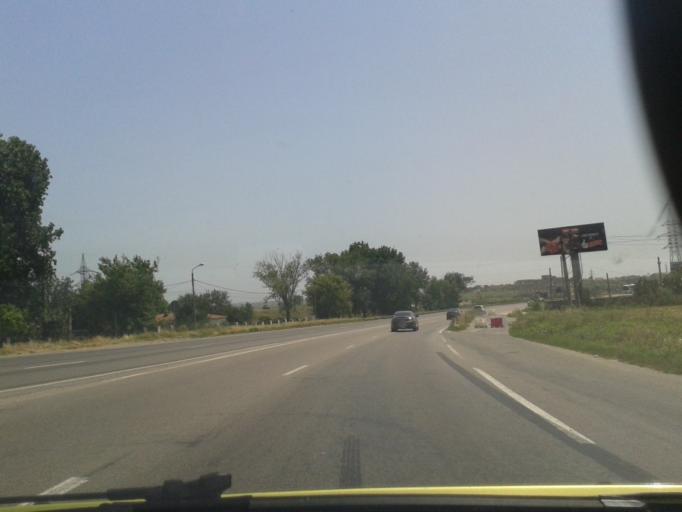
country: RO
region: Constanta
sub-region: Comuna Ovidiu
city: Ovidiu
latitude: 44.2737
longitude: 28.5573
